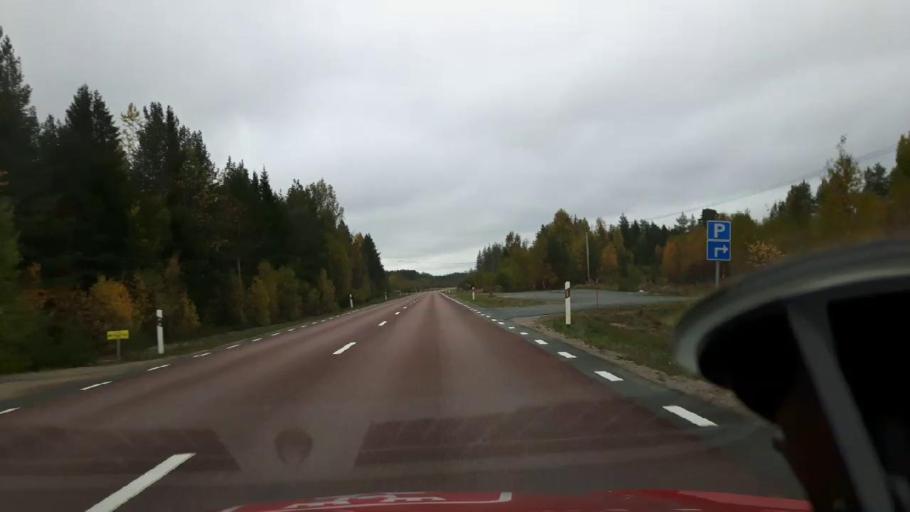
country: SE
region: Jaemtland
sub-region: Harjedalens Kommun
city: Sveg
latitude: 62.2598
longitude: 14.8168
